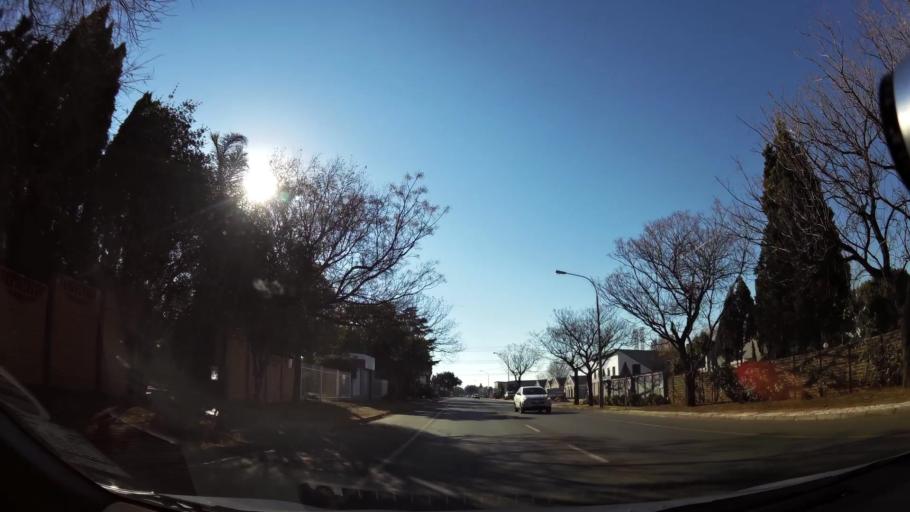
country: ZA
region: Gauteng
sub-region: Ekurhuleni Metropolitan Municipality
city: Germiston
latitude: -26.2856
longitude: 28.1092
